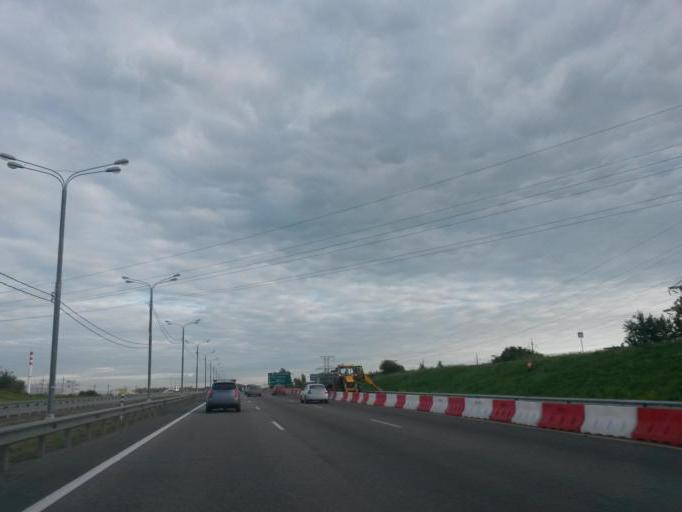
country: RU
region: Moskovskaya
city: Vostryakovo
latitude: 55.3782
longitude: 37.7788
